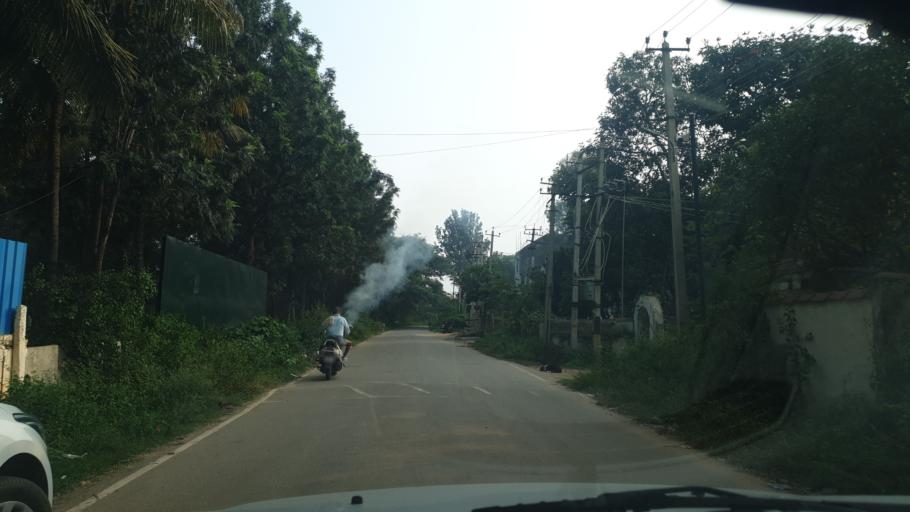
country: IN
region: Karnataka
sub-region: Bangalore Urban
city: Yelahanka
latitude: 13.0708
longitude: 77.6711
